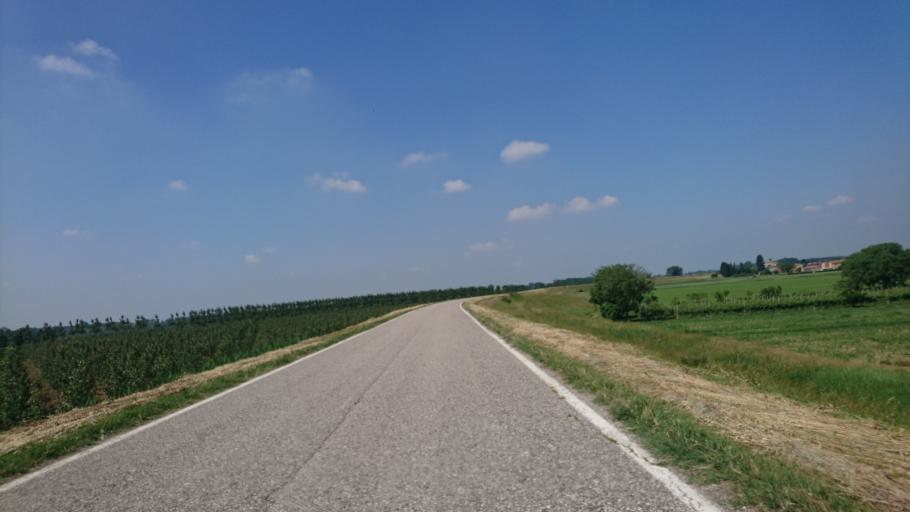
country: IT
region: Lombardy
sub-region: Provincia di Mantova
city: Sustinente
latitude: 45.0672
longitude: 11.0133
